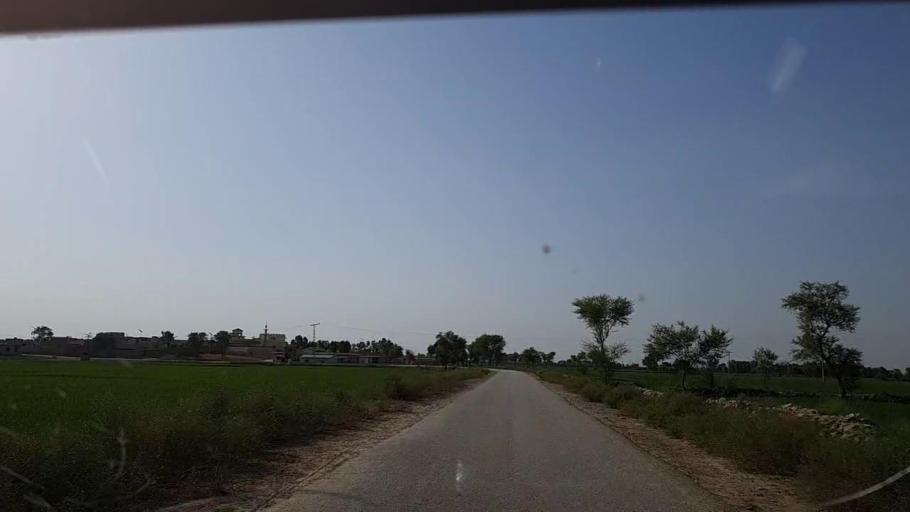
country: PK
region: Sindh
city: Phulji
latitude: 26.9899
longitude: 67.6538
